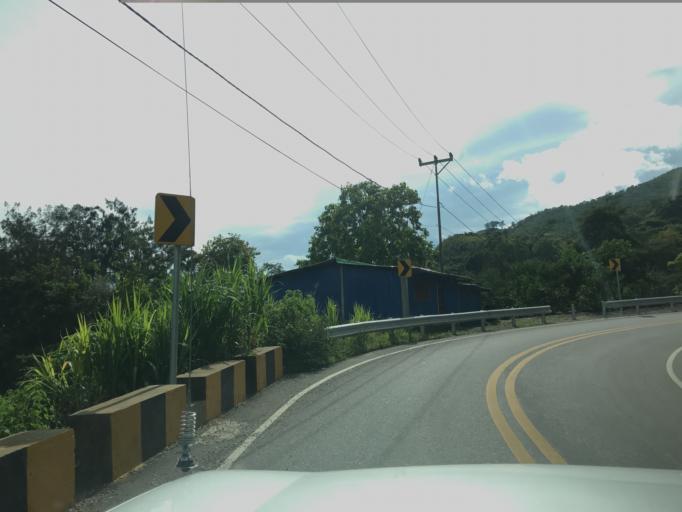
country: TL
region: Aileu
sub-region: Aileu Villa
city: Aileu
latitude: -8.8010
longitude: 125.5787
